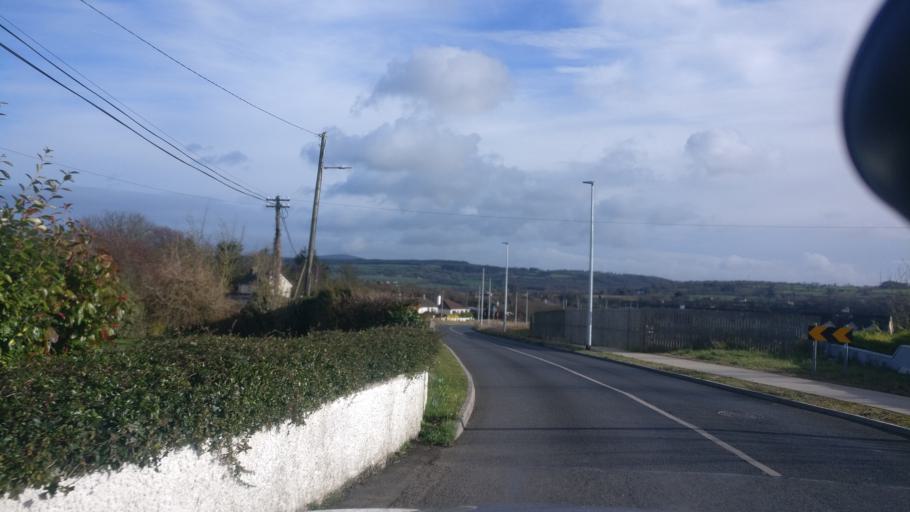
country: IE
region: Leinster
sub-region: Kilkenny
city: Thomastown
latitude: 52.5236
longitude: -7.1569
